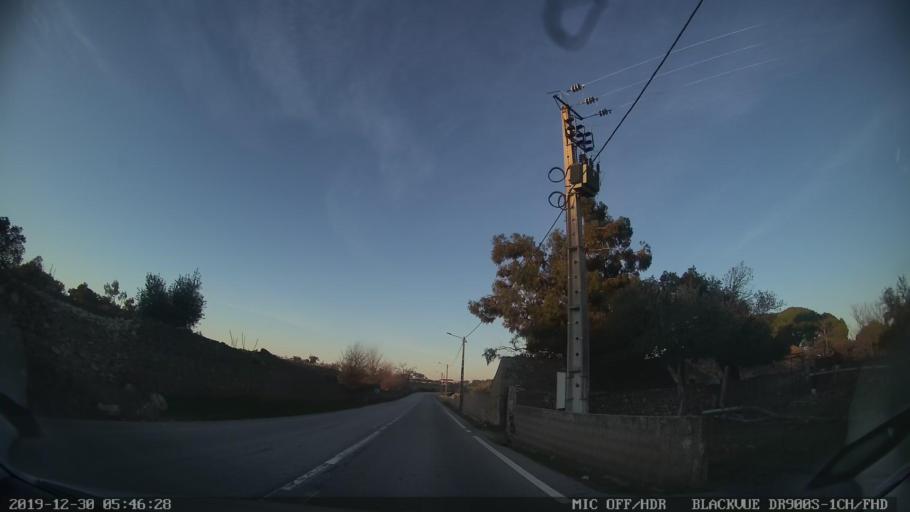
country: PT
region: Castelo Branco
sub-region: Idanha-A-Nova
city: Idanha-a-Nova
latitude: 39.9426
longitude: -7.2362
